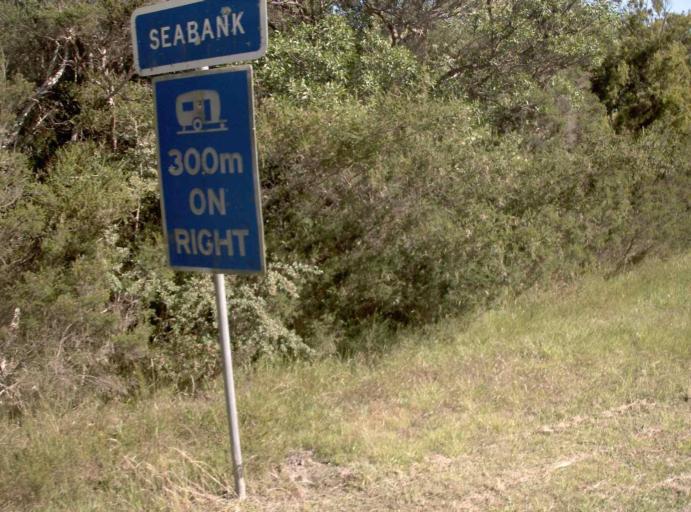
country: AU
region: Victoria
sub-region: Latrobe
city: Traralgon
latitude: -38.6393
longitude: 146.6723
